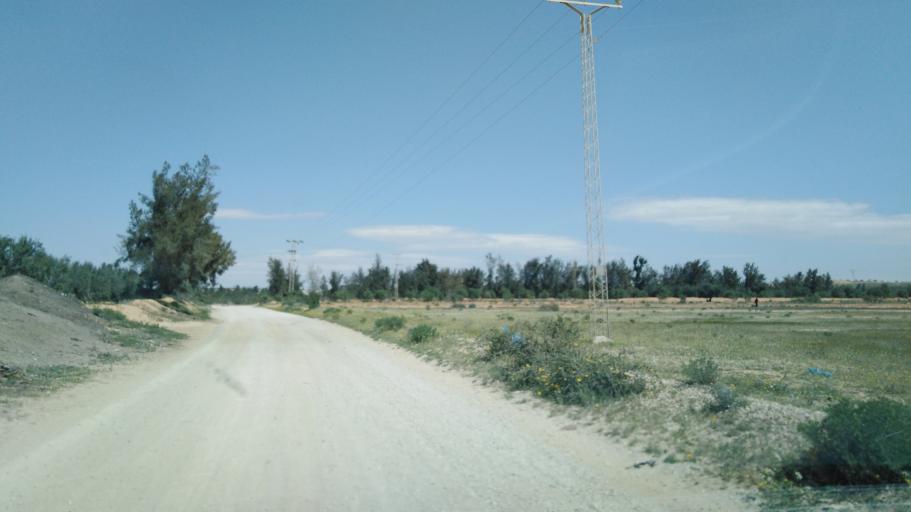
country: TN
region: Safaqis
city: Sfax
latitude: 34.7601
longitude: 10.5286
